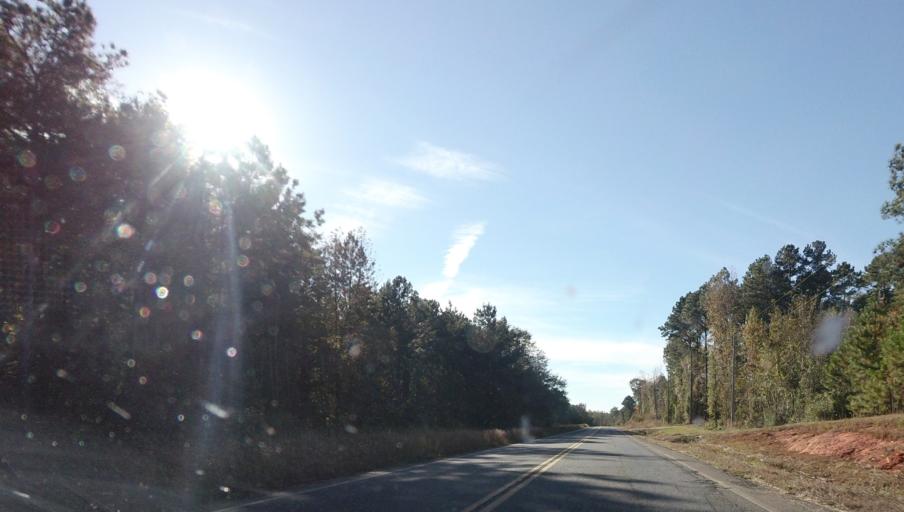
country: US
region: Georgia
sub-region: Talbot County
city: Talbotton
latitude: 32.6809
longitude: -84.5802
